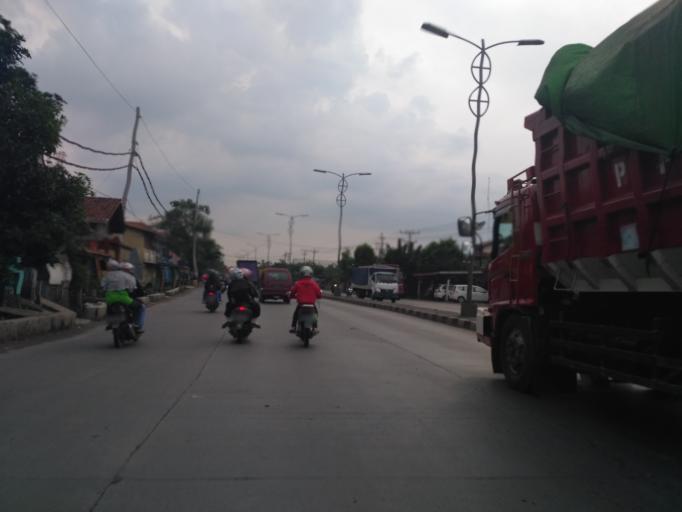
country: ID
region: Central Java
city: Semarang
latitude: -6.9725
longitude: 110.3124
